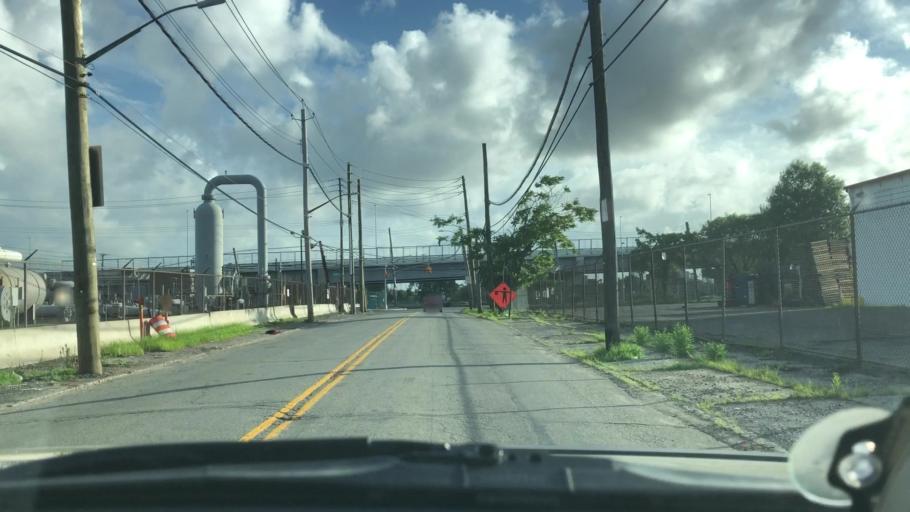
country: US
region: New York
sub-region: Richmond County
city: Bloomfield
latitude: 40.6312
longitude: -74.1854
